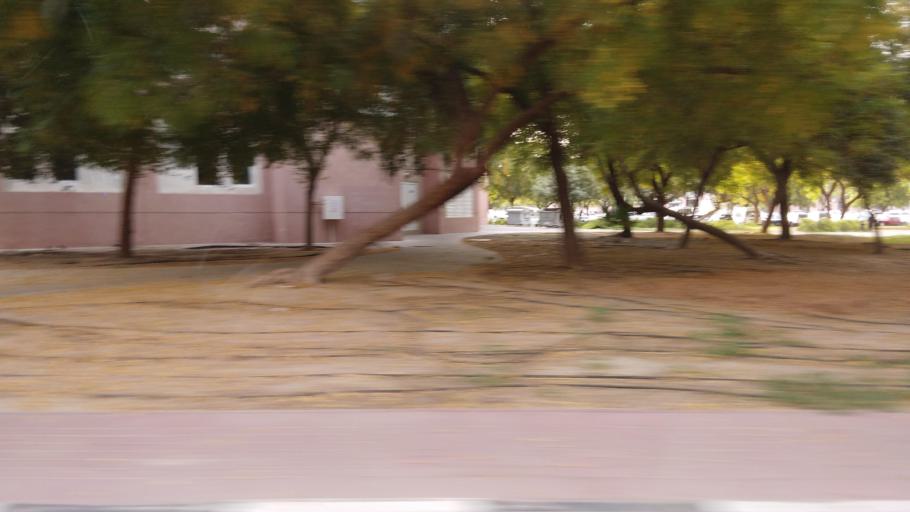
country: AE
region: Dubai
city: Dubai
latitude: 25.0470
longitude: 55.1334
